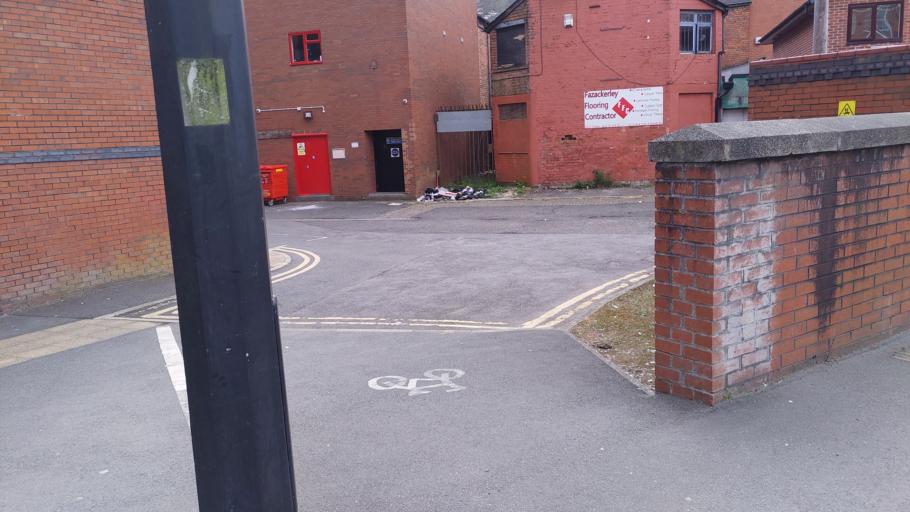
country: GB
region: England
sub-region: Borough of Wigan
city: Ince-in-Makerfield
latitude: 53.5494
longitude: -2.6311
